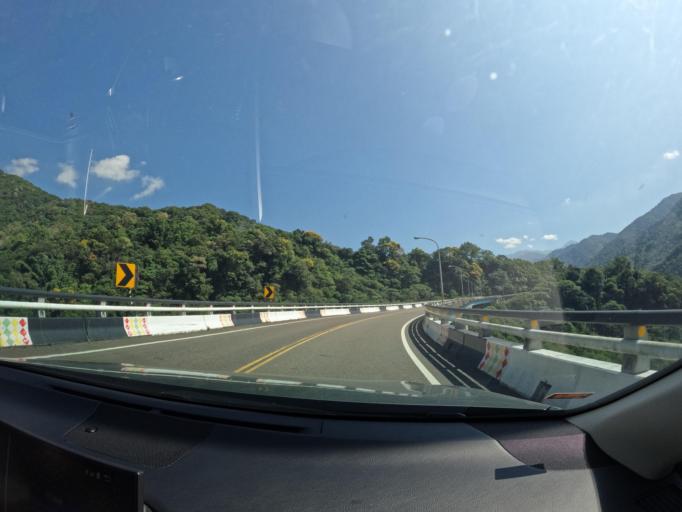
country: TW
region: Taiwan
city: Yujing
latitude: 23.1252
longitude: 120.7097
